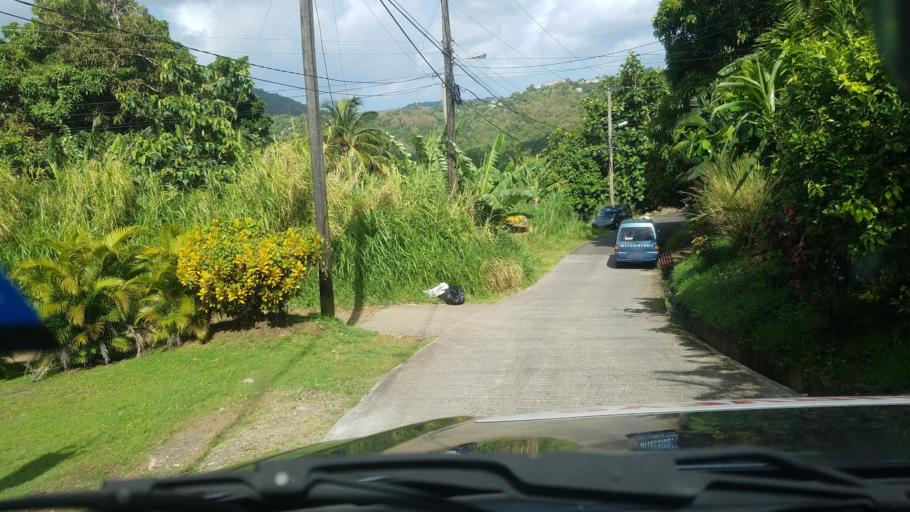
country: LC
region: Castries Quarter
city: Bisee
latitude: 14.0064
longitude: -60.9536
